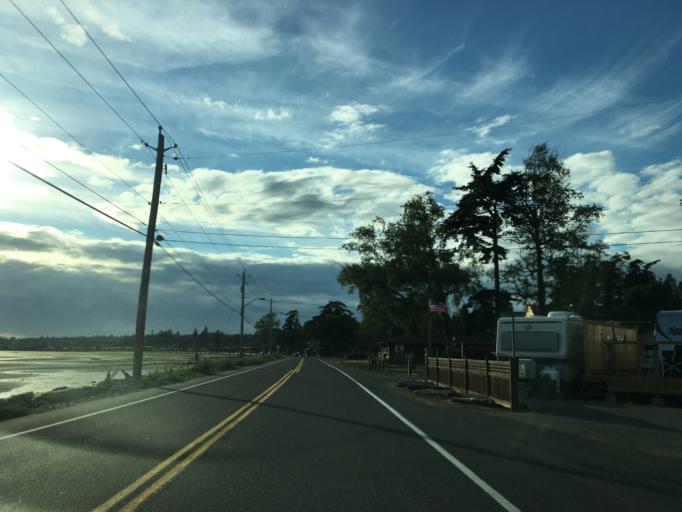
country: US
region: Washington
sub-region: Whatcom County
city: Birch Bay
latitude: 48.9358
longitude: -122.7505
